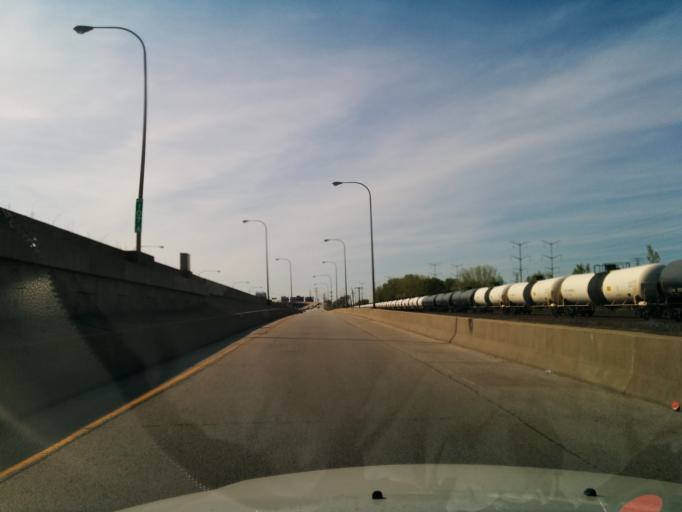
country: US
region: Indiana
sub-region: Lake County
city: Whiting
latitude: 41.7062
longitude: -87.5272
